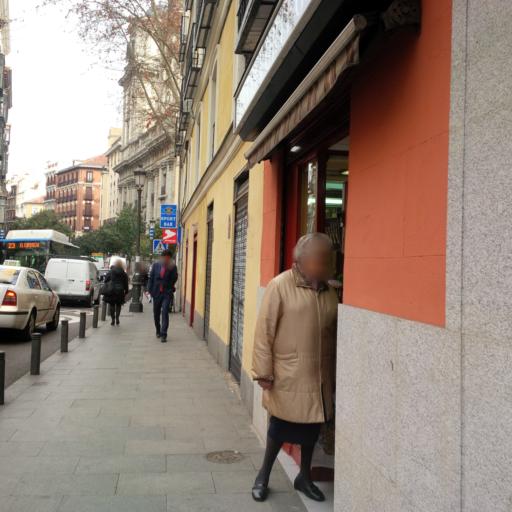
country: ES
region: Madrid
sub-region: Provincia de Madrid
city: Madrid
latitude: 40.4123
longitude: -3.7077
